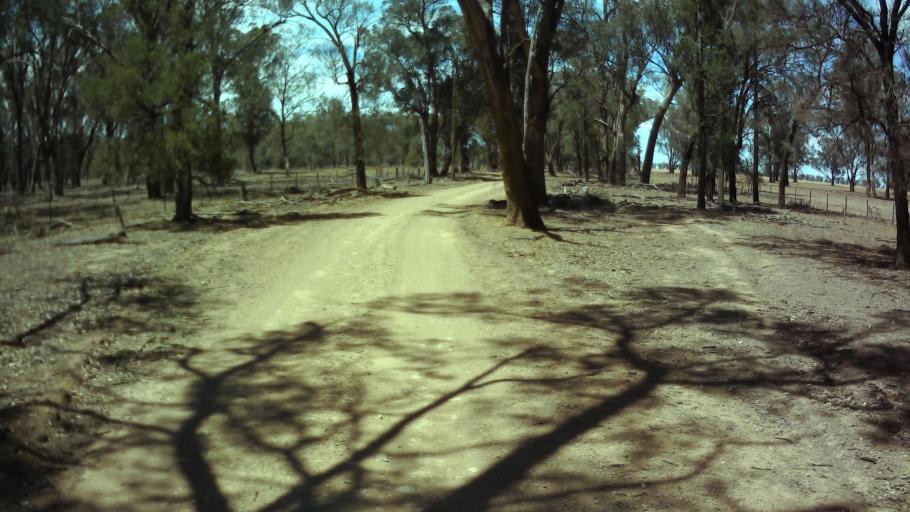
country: AU
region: New South Wales
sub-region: Weddin
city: Grenfell
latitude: -33.9113
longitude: 147.8065
